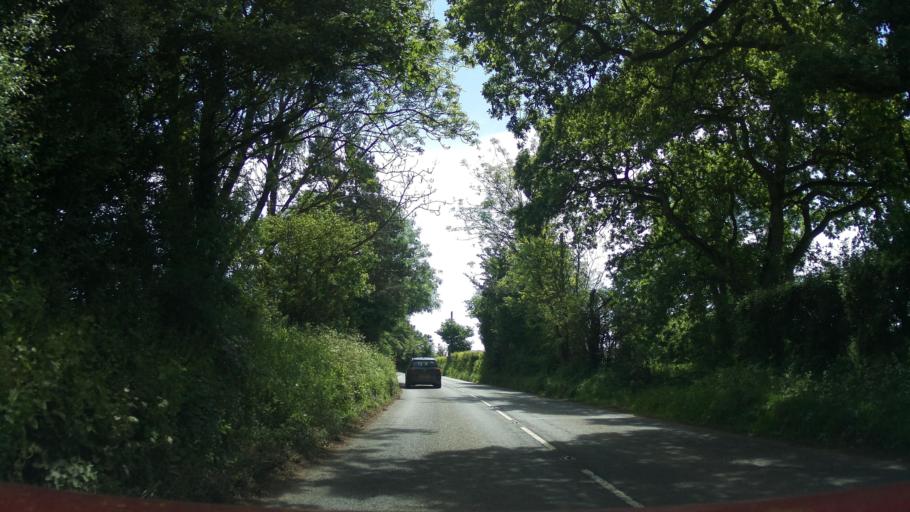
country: GB
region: England
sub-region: Devon
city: Uffculme
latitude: 50.8282
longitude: -3.2987
